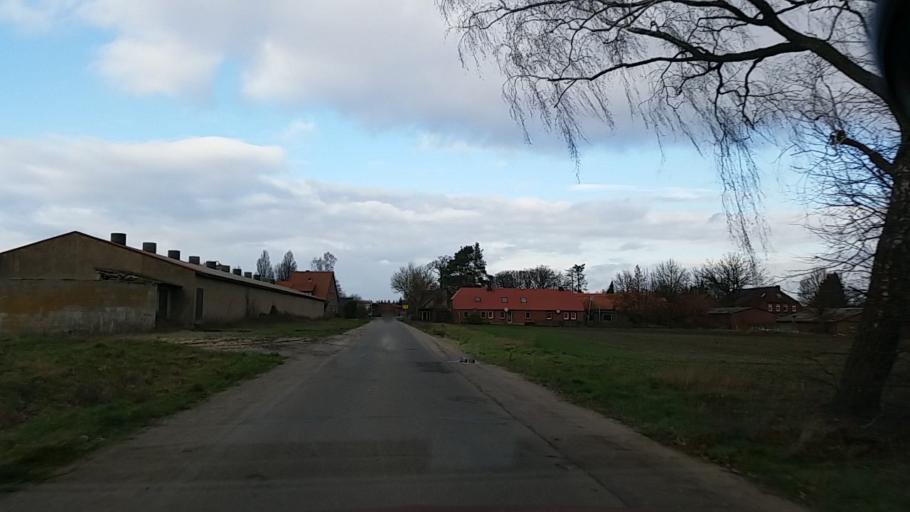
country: DE
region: Lower Saxony
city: Wieren
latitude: 52.8798
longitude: 10.6542
